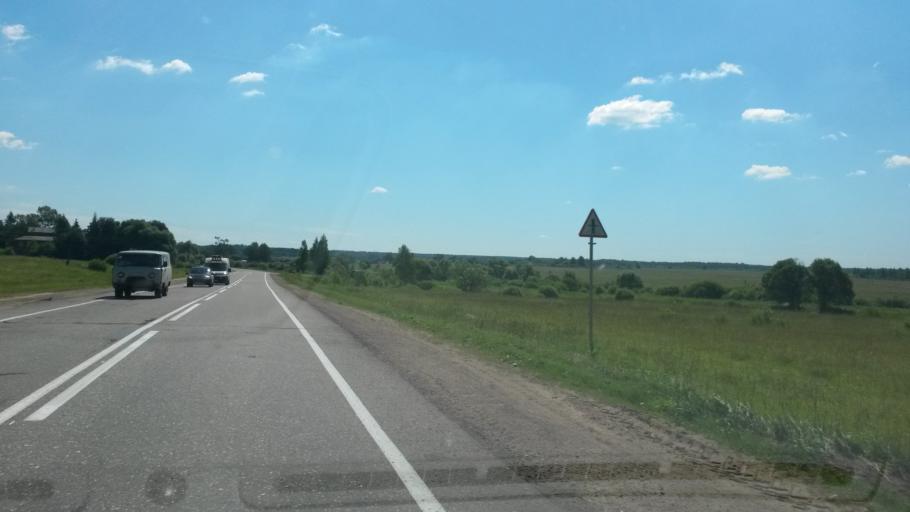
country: RU
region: Jaroslavl
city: Dubki
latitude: 57.2365
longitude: 40.1853
